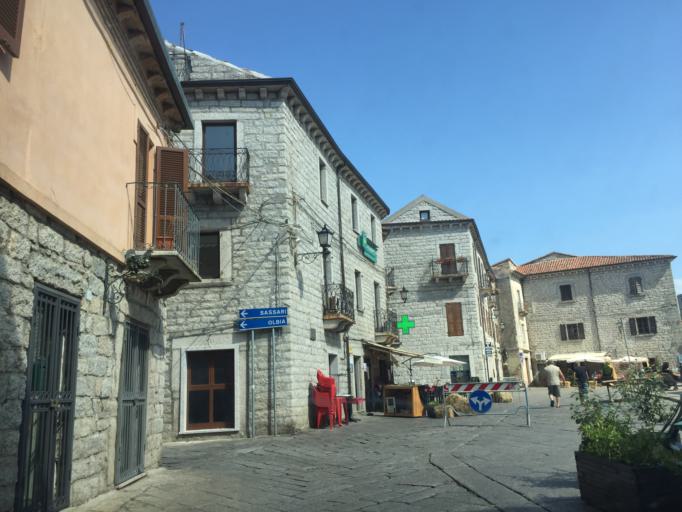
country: IT
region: Sardinia
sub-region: Provincia di Olbia-Tempio
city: Tempio Pausania
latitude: 40.9035
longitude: 9.1037
